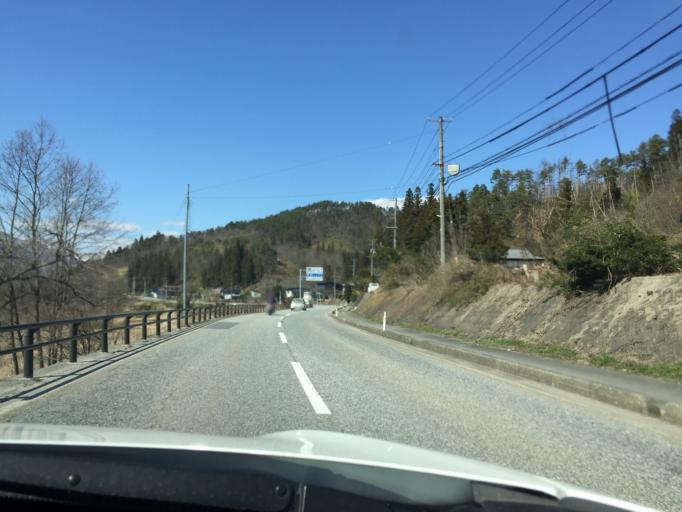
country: JP
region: Yamagata
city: Nagai
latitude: 38.2003
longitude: 140.1038
